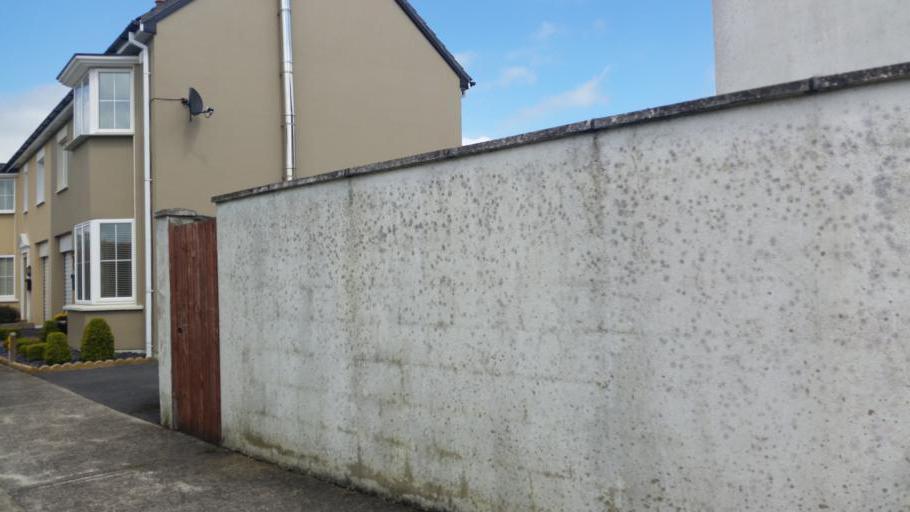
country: IE
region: Leinster
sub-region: Laois
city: Portlaoise
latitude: 53.0494
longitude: -7.3249
